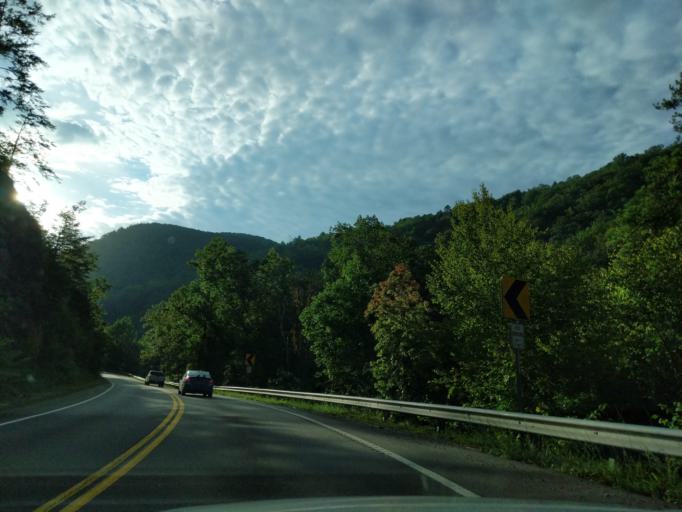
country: US
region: Tennessee
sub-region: Polk County
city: Benton
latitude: 35.0818
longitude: -84.5289
